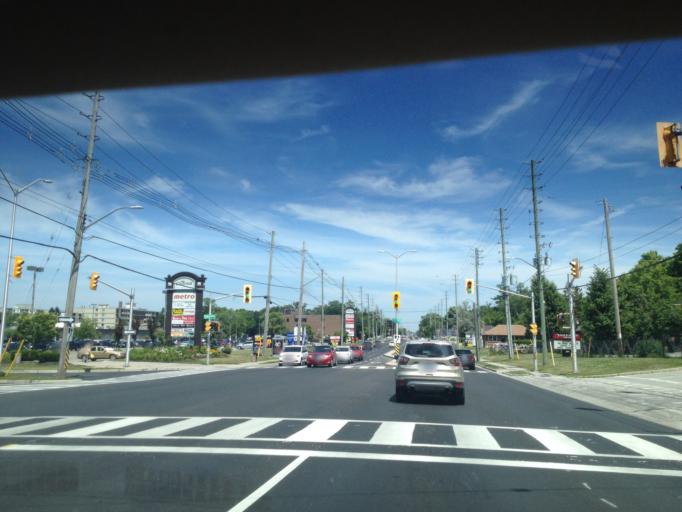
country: CA
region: Ontario
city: London
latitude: 42.9885
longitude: -81.2766
